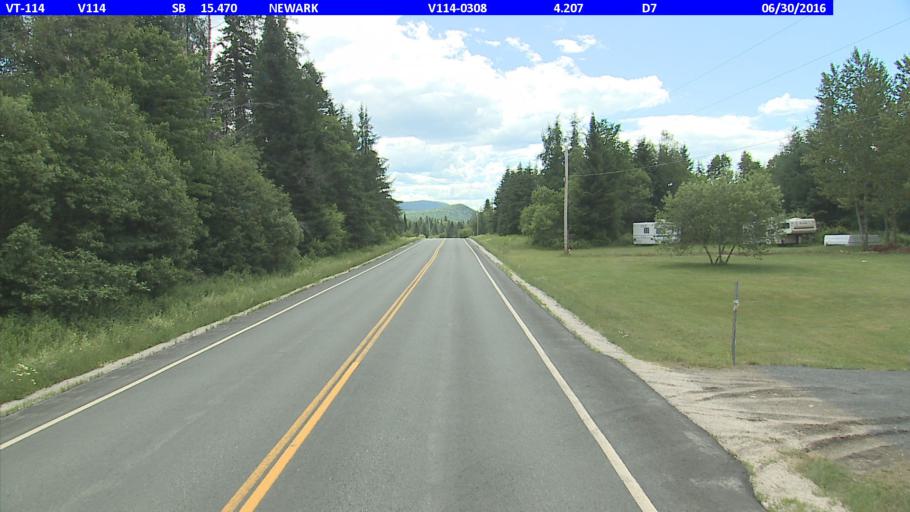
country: US
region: Vermont
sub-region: Caledonia County
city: Lyndonville
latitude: 44.7265
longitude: -71.8744
